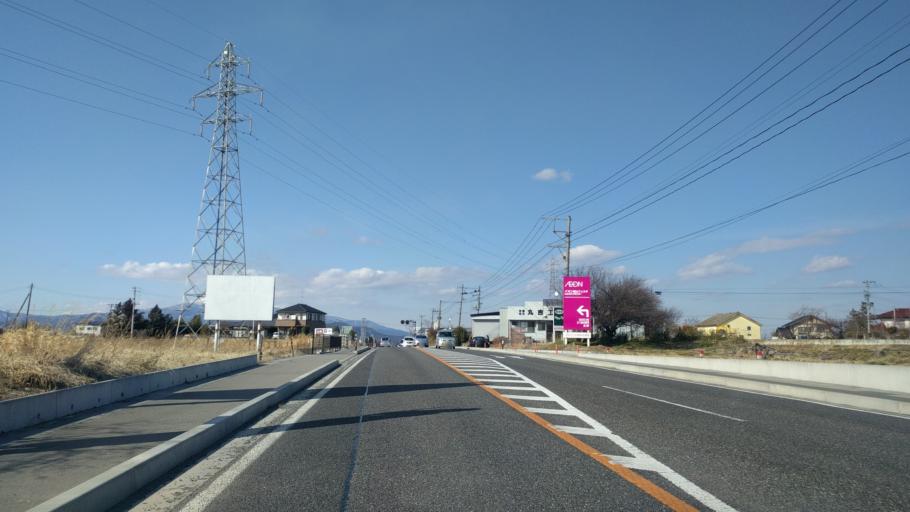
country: JP
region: Fukushima
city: Koriyama
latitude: 37.4358
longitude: 140.3807
